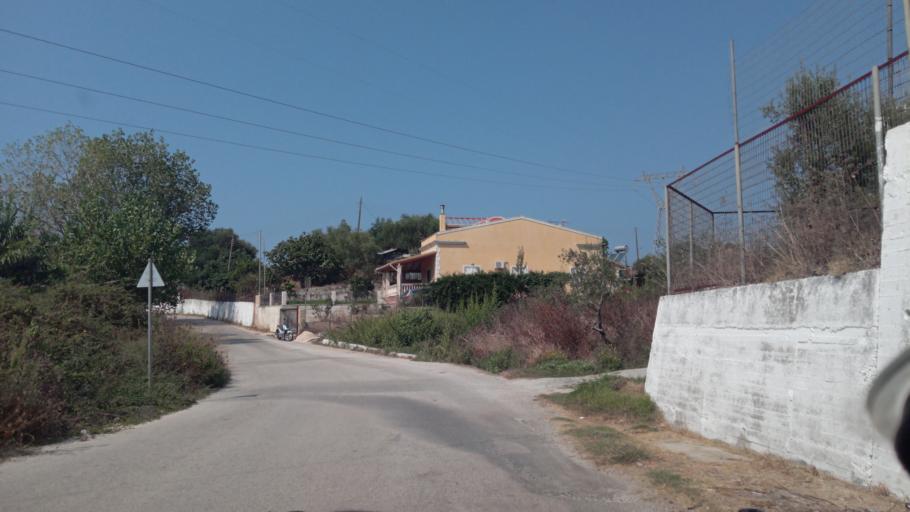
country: GR
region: Ionian Islands
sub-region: Nomos Kerkyras
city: Perivoli
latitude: 39.4122
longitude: 20.0239
